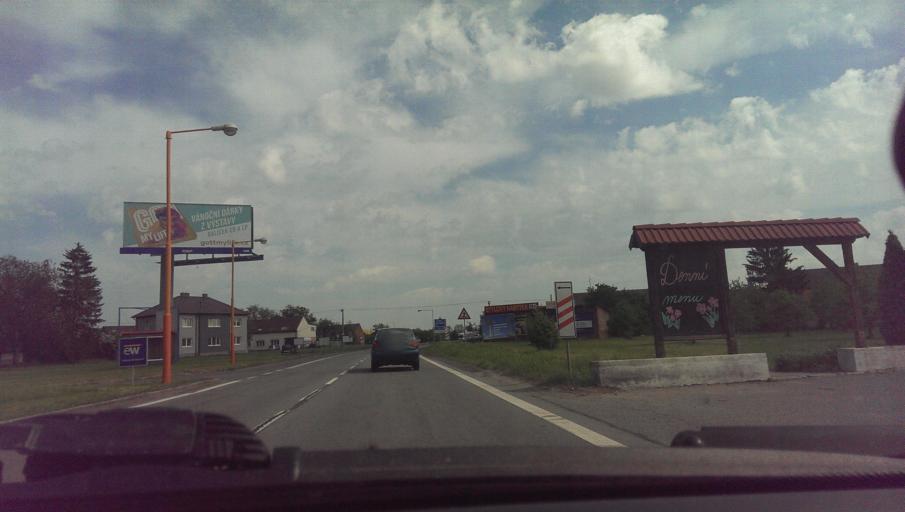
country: CZ
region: Zlin
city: Babice
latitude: 49.1229
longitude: 17.4759
